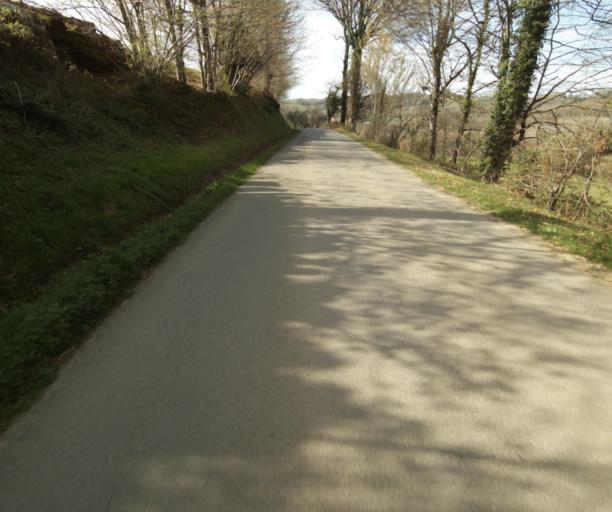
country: FR
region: Limousin
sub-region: Departement de la Correze
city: Naves
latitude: 45.3082
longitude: 1.7334
